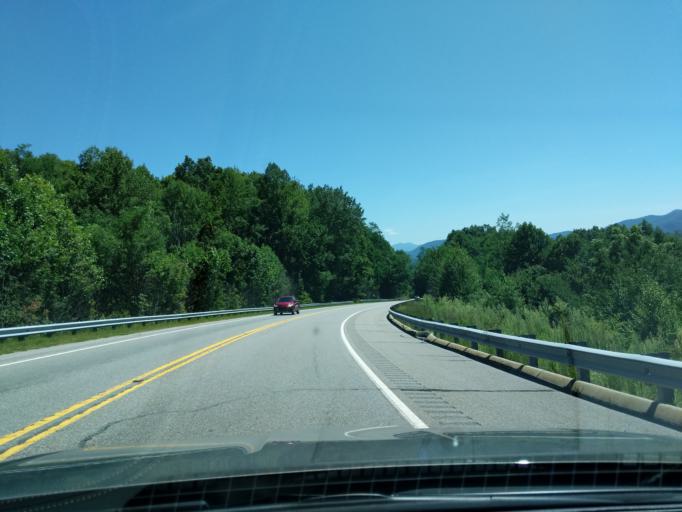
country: US
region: North Carolina
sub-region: Macon County
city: Franklin
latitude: 35.1308
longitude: -83.5341
